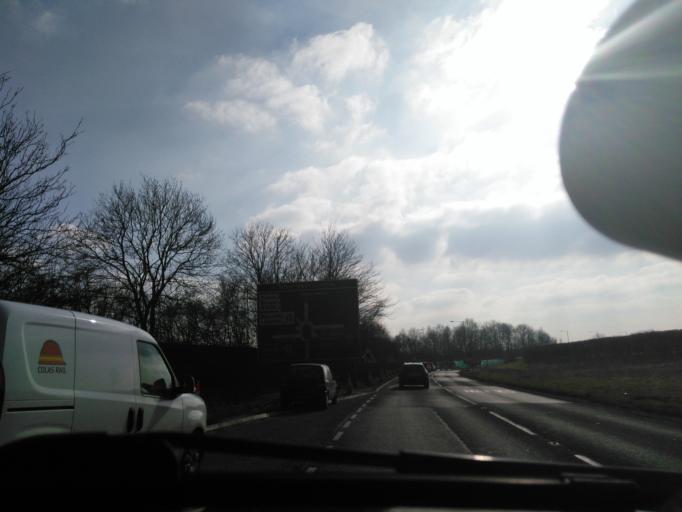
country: GB
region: England
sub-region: Wiltshire
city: Chippenham
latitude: 51.5178
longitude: -2.1208
